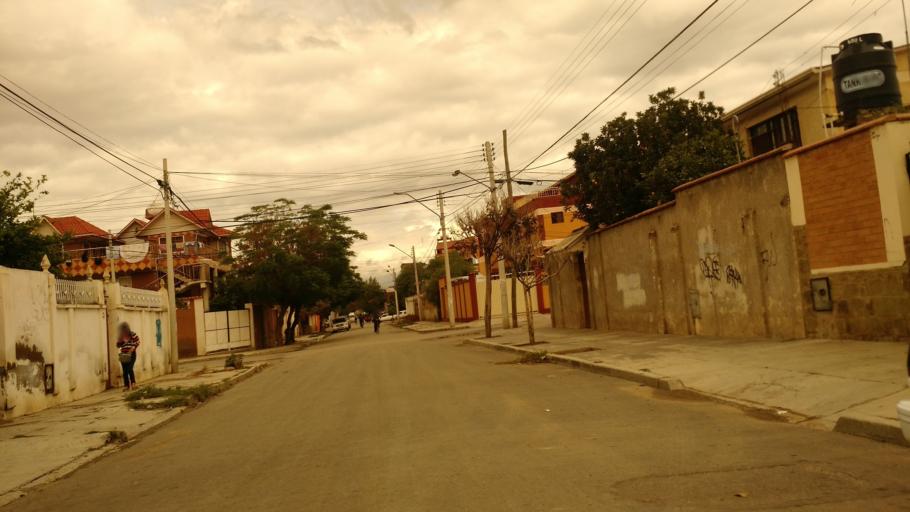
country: BO
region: Cochabamba
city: Cochabamba
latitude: -17.4245
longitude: -66.1570
